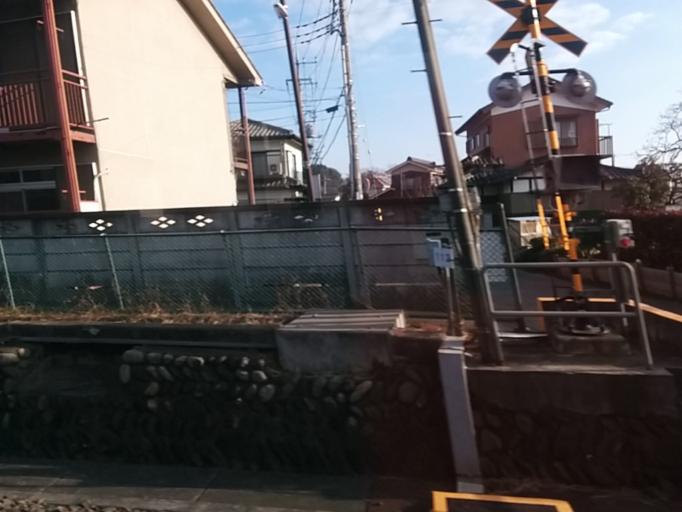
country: JP
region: Saitama
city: Oi
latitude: 35.8519
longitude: 139.5311
